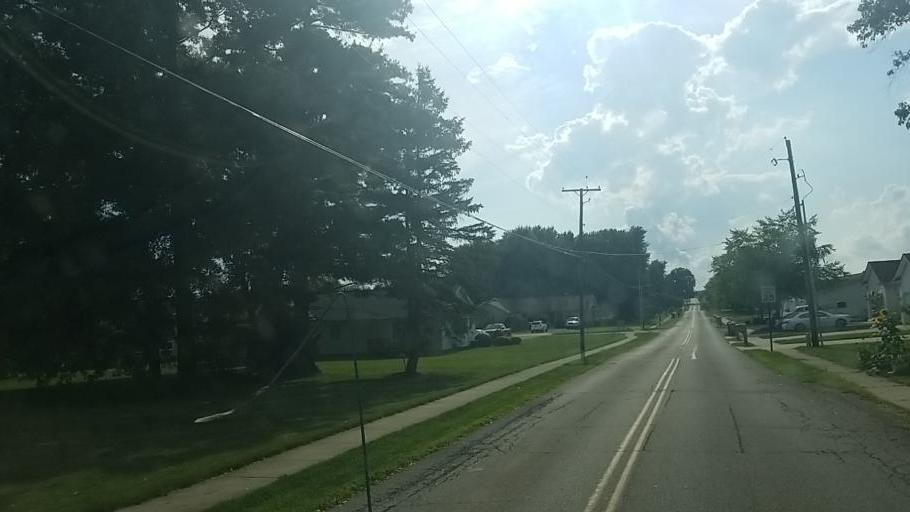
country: US
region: Ohio
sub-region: Wayne County
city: Smithville
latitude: 40.8659
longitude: -81.8619
